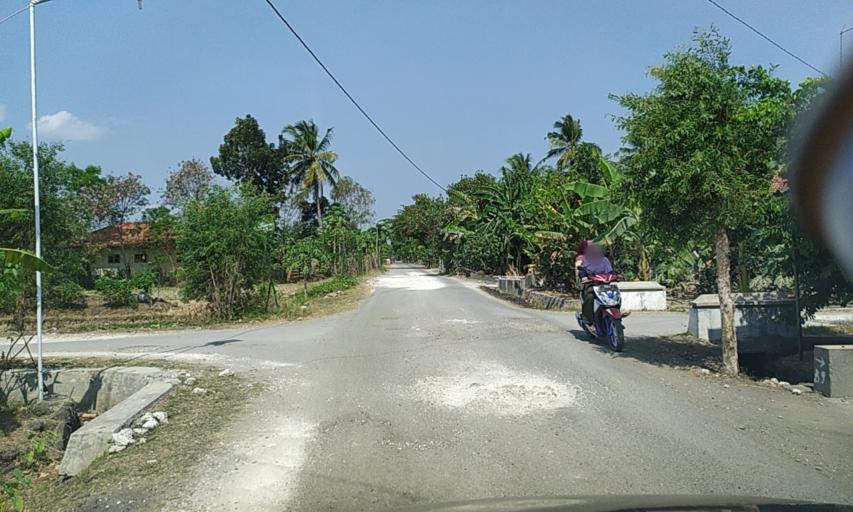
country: ID
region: Central Java
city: Mulyosari
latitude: -7.5029
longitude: 108.7941
